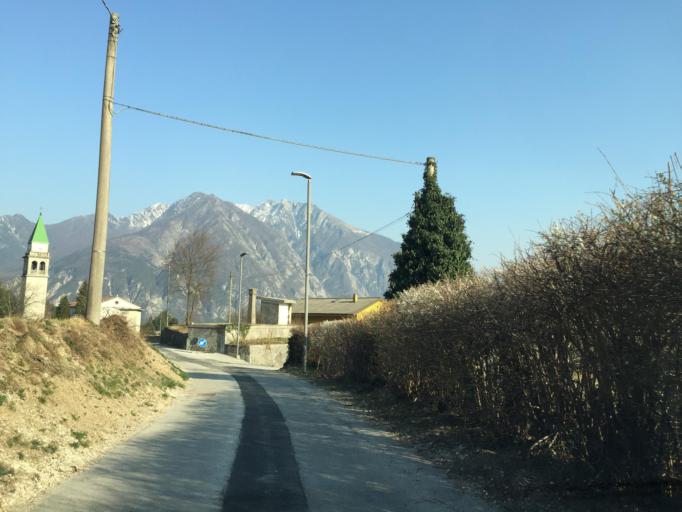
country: IT
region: Friuli Venezia Giulia
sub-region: Provincia di Udine
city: Amaro
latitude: 46.3763
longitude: 13.0928
